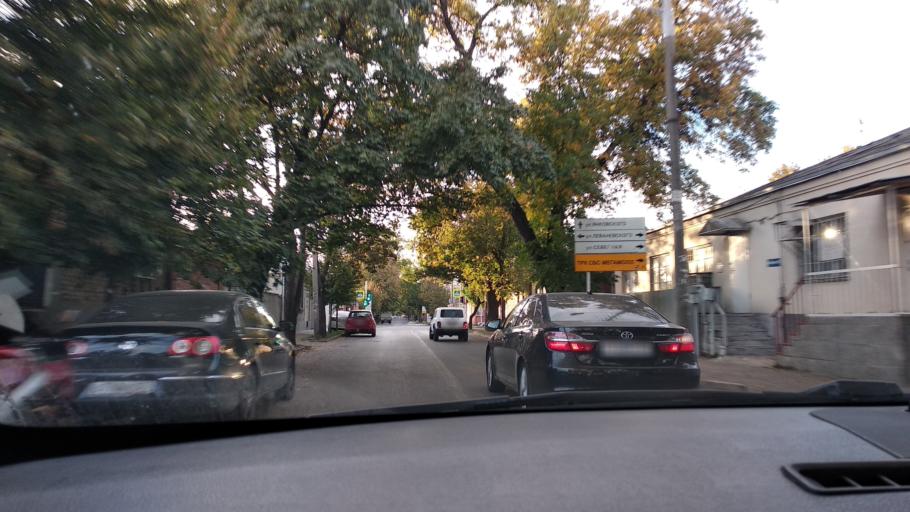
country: RU
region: Krasnodarskiy
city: Krasnodar
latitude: 45.0265
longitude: 38.9831
